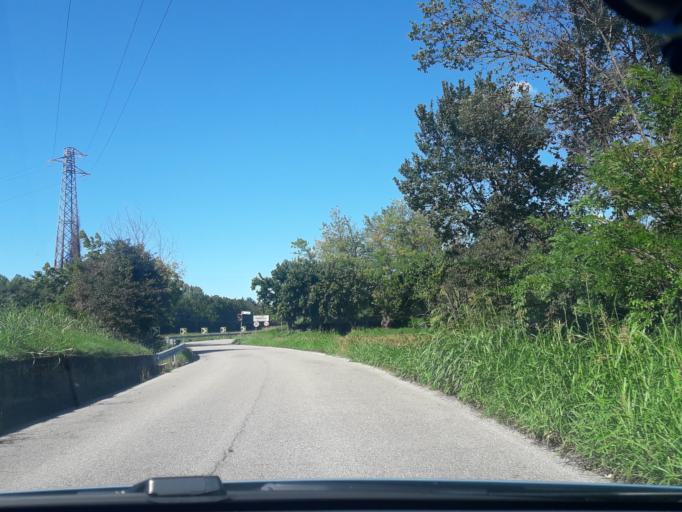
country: IT
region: Friuli Venezia Giulia
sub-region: Provincia di Udine
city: Reana del Roiale
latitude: 46.1382
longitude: 13.2164
